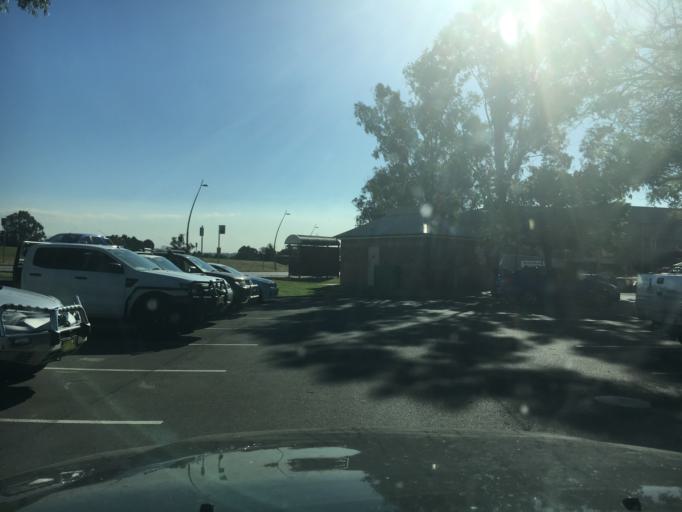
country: AU
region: New South Wales
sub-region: Singleton
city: Singleton
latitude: -32.5647
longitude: 151.1666
